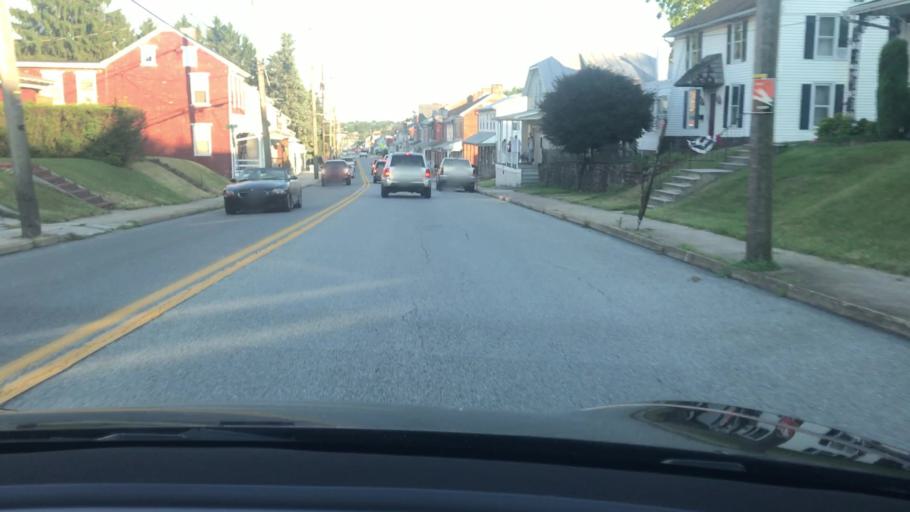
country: US
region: Pennsylvania
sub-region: York County
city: Dover
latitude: 40.0048
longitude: -76.8543
